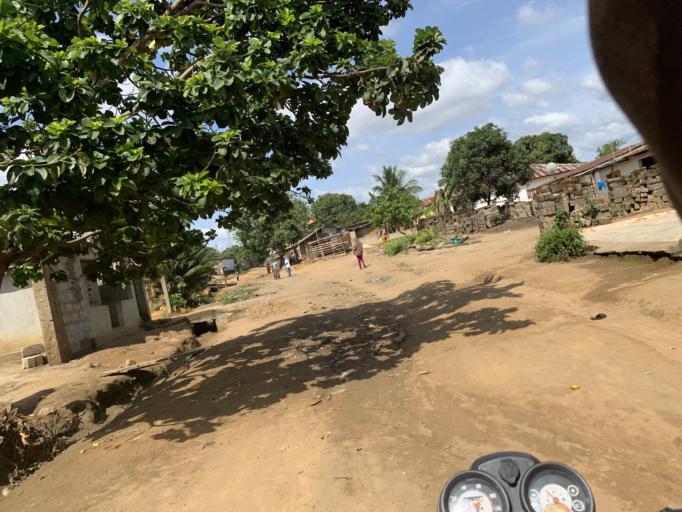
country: SL
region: Western Area
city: Waterloo
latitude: 8.3346
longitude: -13.0459
